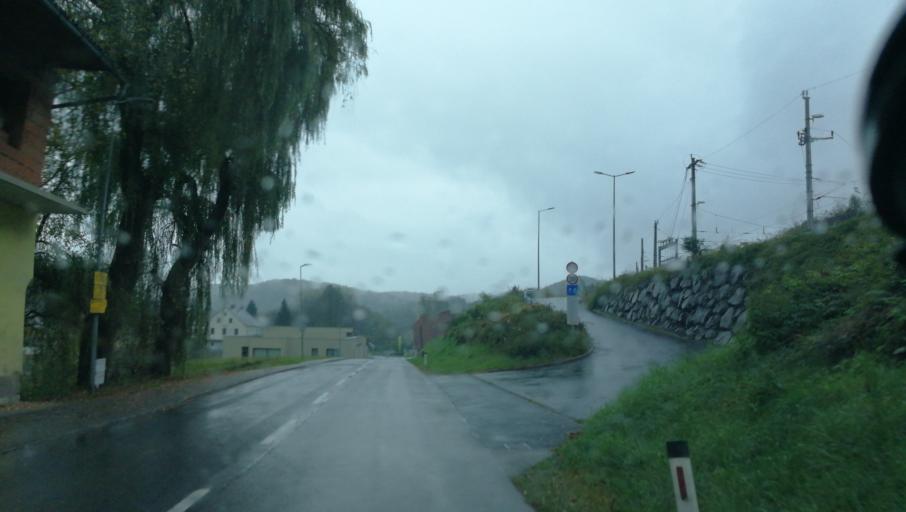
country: AT
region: Styria
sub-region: Politischer Bezirk Leibnitz
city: Spielfeld
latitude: 46.7096
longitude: 15.6300
